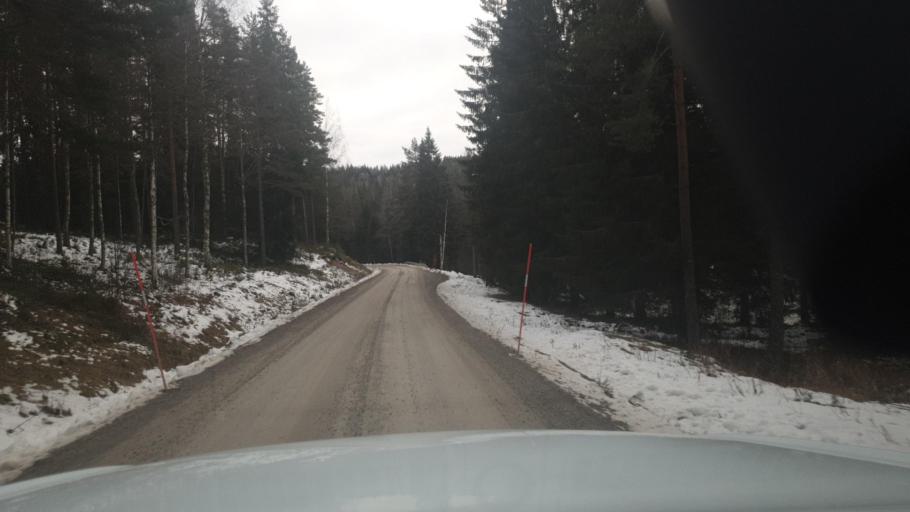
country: SE
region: Vaermland
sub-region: Sunne Kommun
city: Sunne
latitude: 59.8535
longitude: 12.9066
